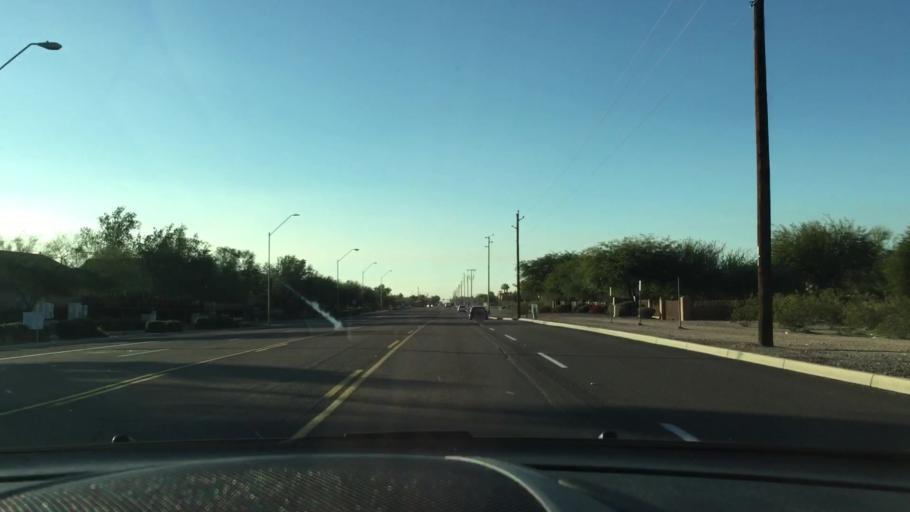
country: US
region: Arizona
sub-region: Maricopa County
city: Sun City
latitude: 33.7049
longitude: -112.2032
